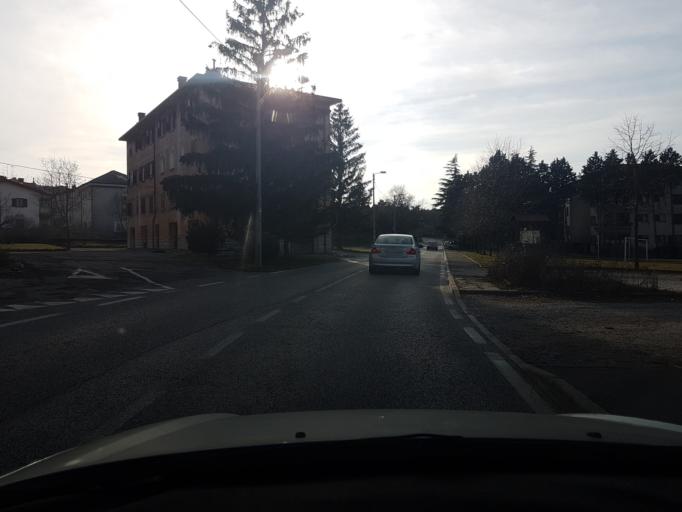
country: IT
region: Friuli Venezia Giulia
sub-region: Provincia di Trieste
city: Villa Opicina
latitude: 45.6920
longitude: 13.7778
